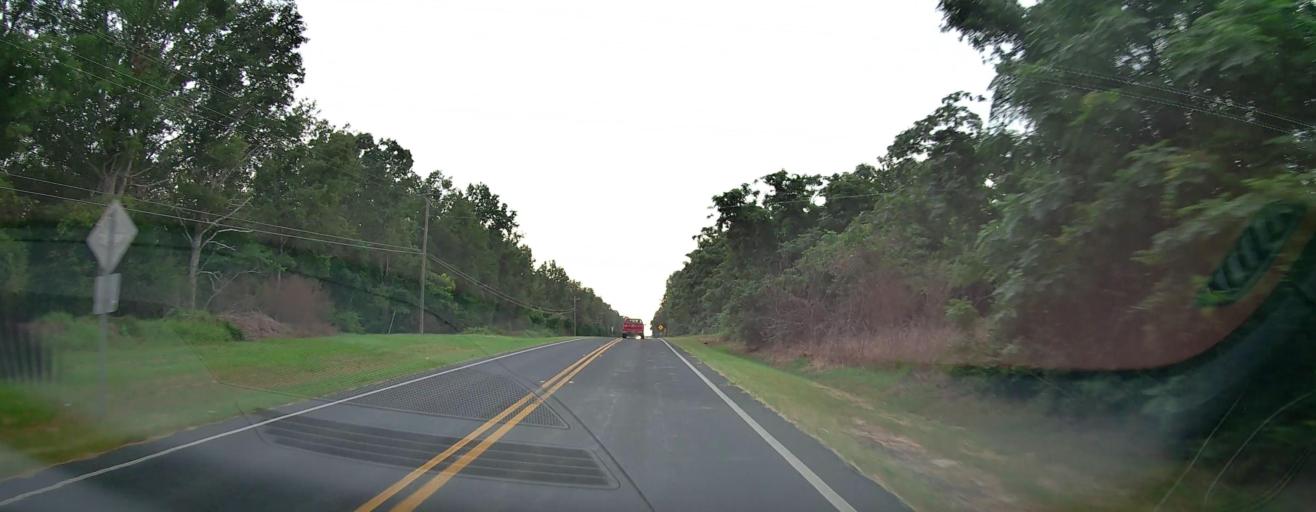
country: US
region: Georgia
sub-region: Laurens County
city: East Dublin
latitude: 32.5334
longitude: -82.8376
